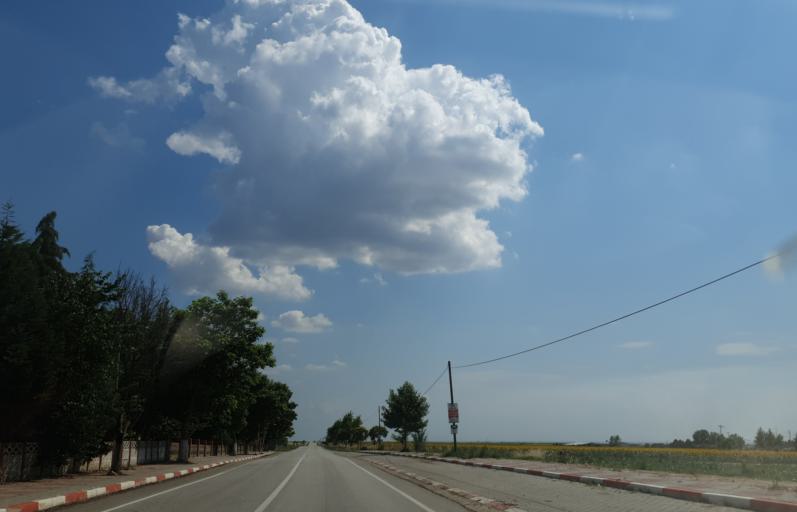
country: TR
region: Kirklareli
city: Buyukkaristiran
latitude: 41.4350
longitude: 27.5836
